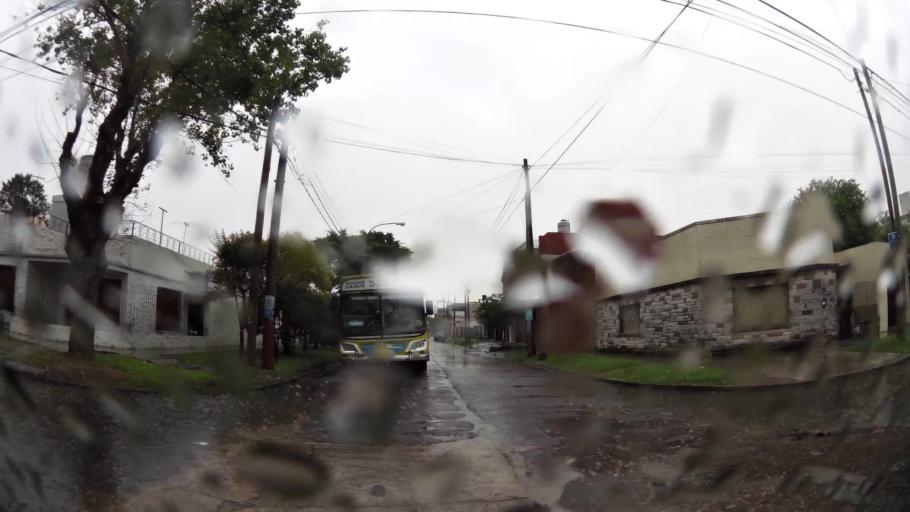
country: AR
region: Buenos Aires
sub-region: Partido de Lanus
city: Lanus
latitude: -34.7138
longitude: -58.4138
